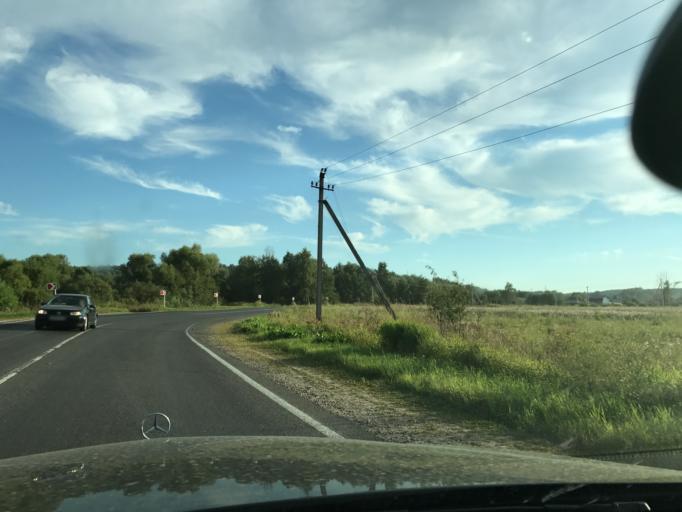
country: RU
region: Vladimir
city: Raduzhnyy
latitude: 56.0252
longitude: 40.3367
